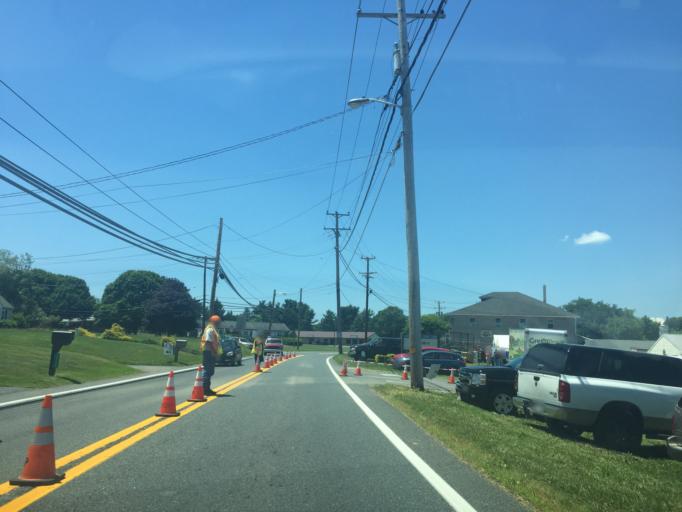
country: US
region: Maryland
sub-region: Harford County
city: Jarrettsville
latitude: 39.6025
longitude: -76.4824
